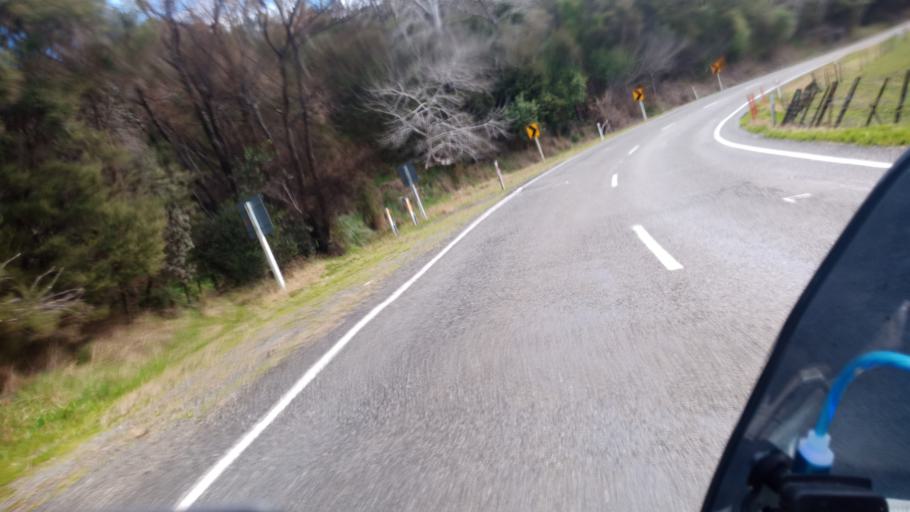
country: NZ
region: Gisborne
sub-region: Gisborne District
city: Gisborne
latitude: -37.8629
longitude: 178.3242
